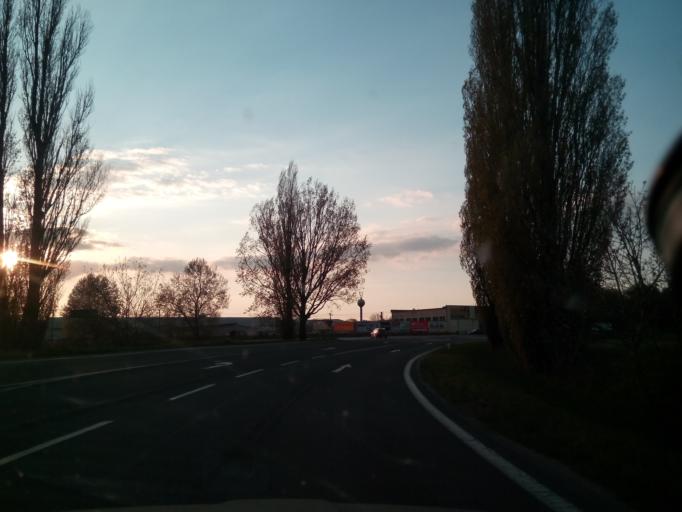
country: SK
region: Trnavsky
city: Vrbove
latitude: 48.5919
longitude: 17.7489
